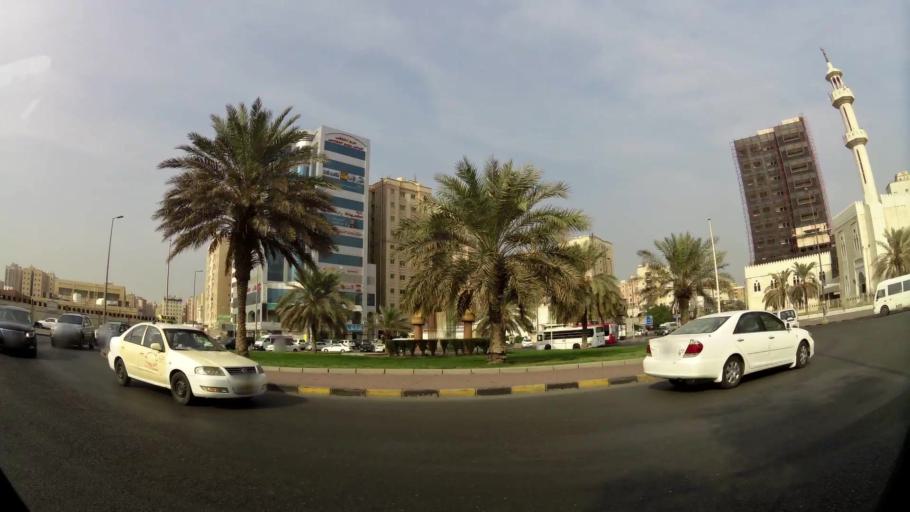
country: KW
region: Al Farwaniyah
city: Al Farwaniyah
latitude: 29.2813
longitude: 47.9603
